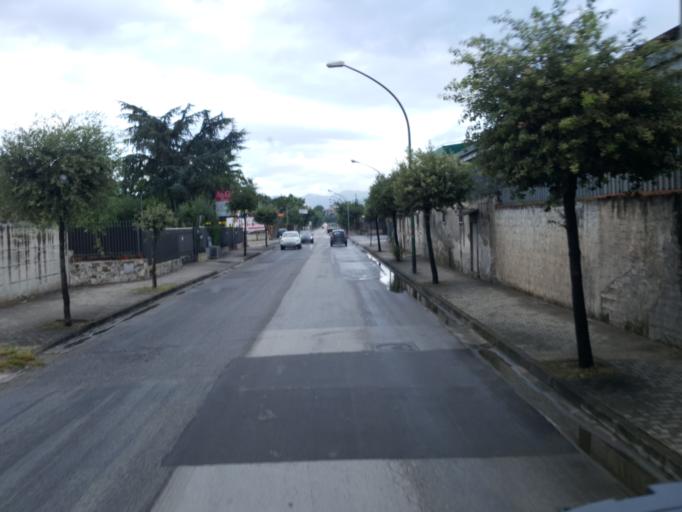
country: IT
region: Campania
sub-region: Provincia di Napoli
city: Palma Campania
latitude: 40.8619
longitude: 14.5486
